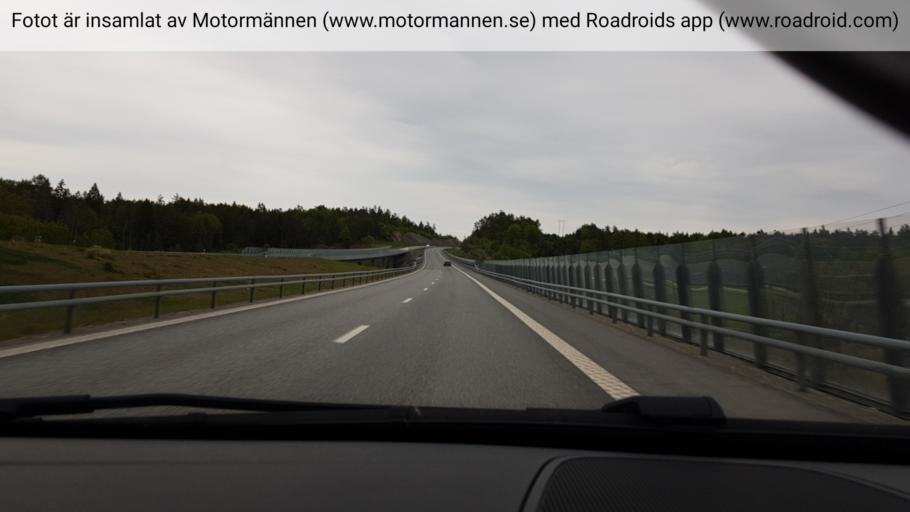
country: SE
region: Stockholm
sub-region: Nynashamns Kommun
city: Osmo
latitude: 59.0538
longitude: 18.0016
